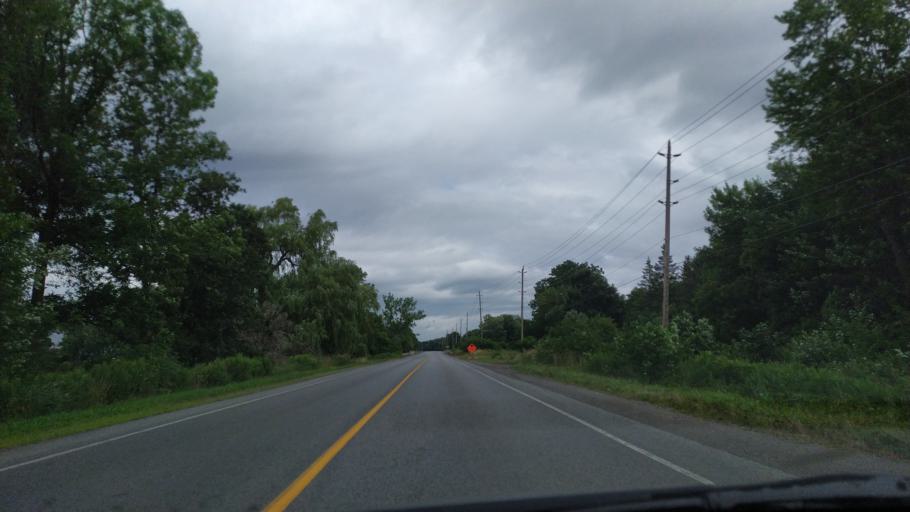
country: CA
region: Ontario
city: Quinte West
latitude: 43.9945
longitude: -77.5179
